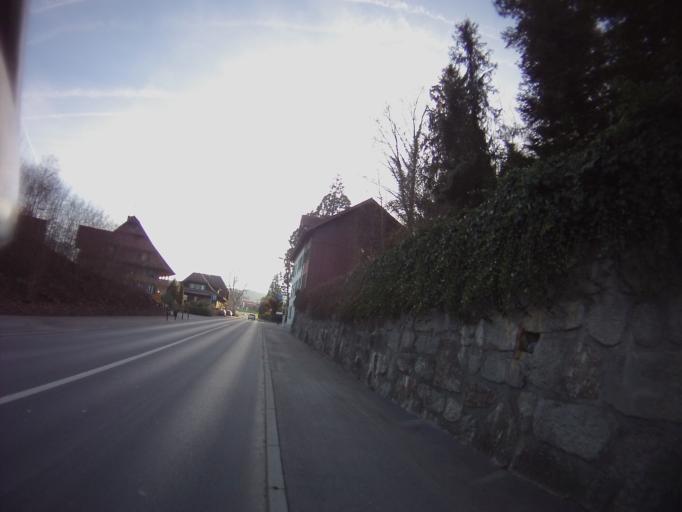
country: CH
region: Zug
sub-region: Zug
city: Cham
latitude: 47.1645
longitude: 8.4468
